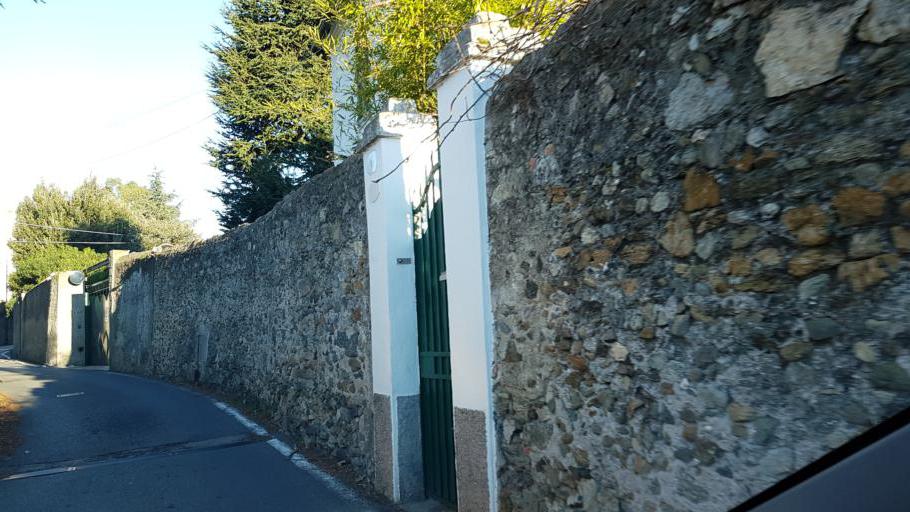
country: IT
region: Liguria
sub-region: Provincia di Savona
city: Savona
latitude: 44.2971
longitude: 8.4522
